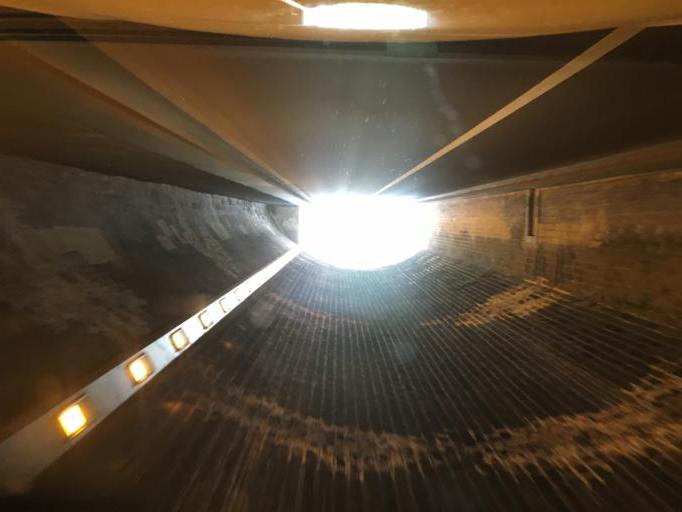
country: FR
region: Lorraine
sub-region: Departement de Meurthe-et-Moselle
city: Jarville-la-Malgrange
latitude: 48.6743
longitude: 6.1951
